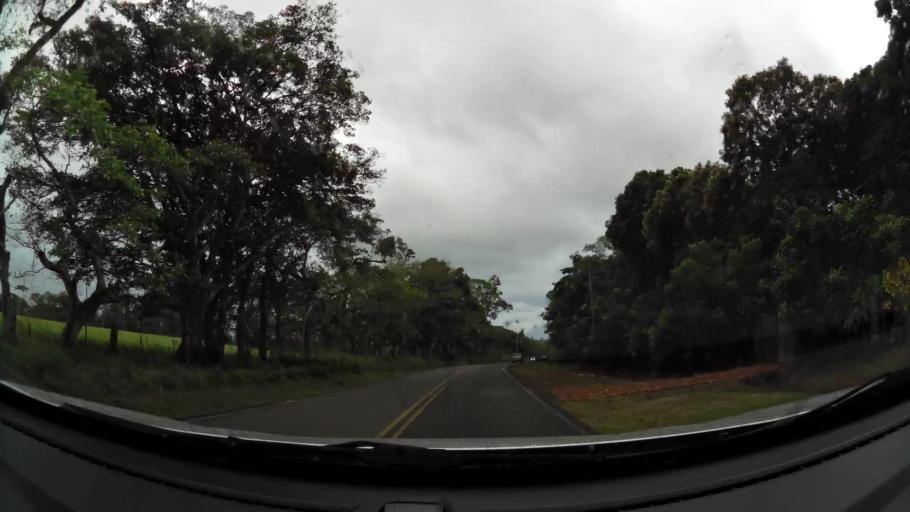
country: CR
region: Puntarenas
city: Esparza
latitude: 9.9900
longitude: -84.6302
